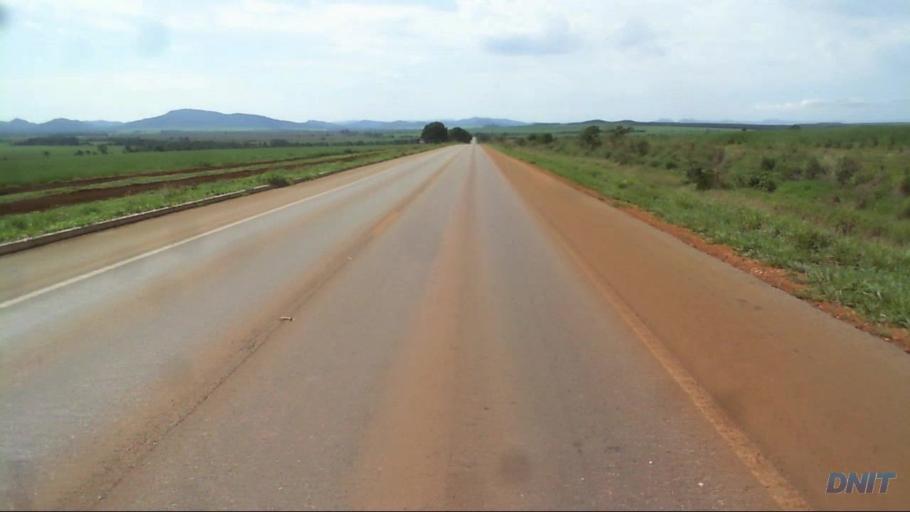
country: BR
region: Goias
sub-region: Barro Alto
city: Barro Alto
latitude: -15.0298
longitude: -48.8940
